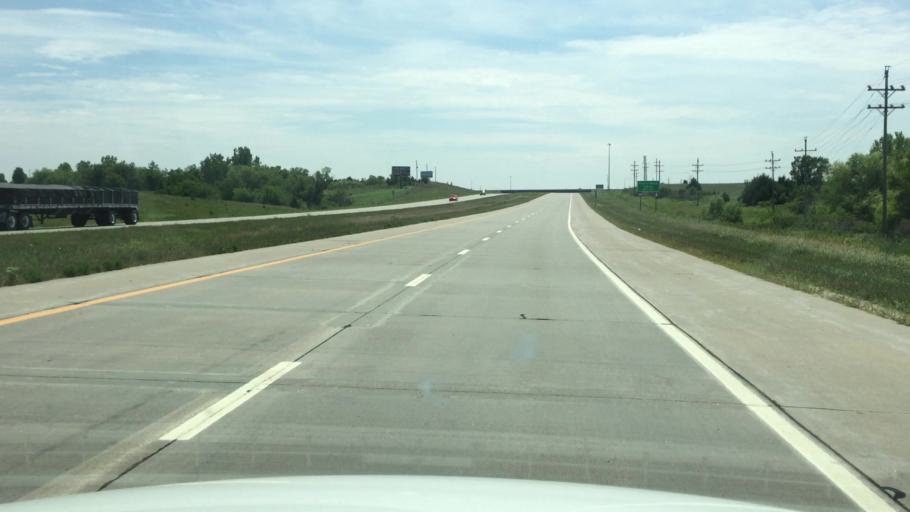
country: US
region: Kansas
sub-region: Jackson County
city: Holton
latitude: 39.3267
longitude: -95.7202
